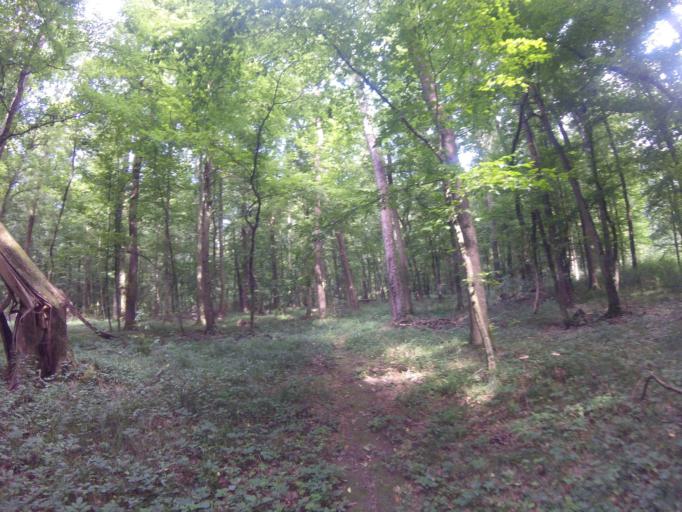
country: HU
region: Zala
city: Lenti
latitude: 46.6311
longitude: 16.5557
